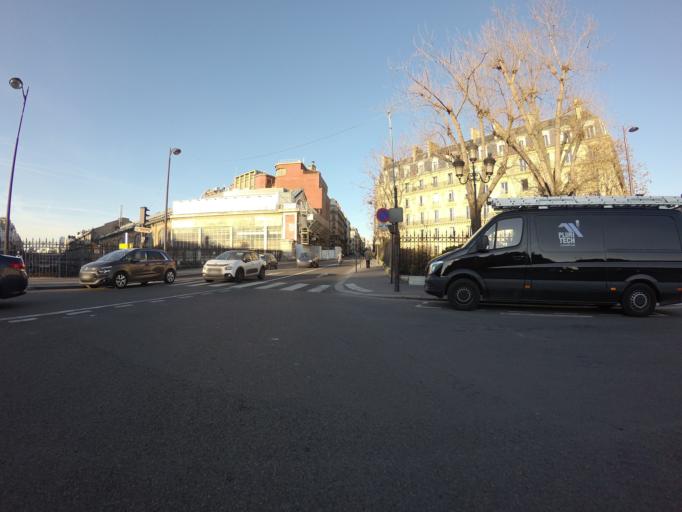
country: FR
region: Ile-de-France
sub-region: Paris
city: Saint-Ouen
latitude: 48.8797
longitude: 2.3235
